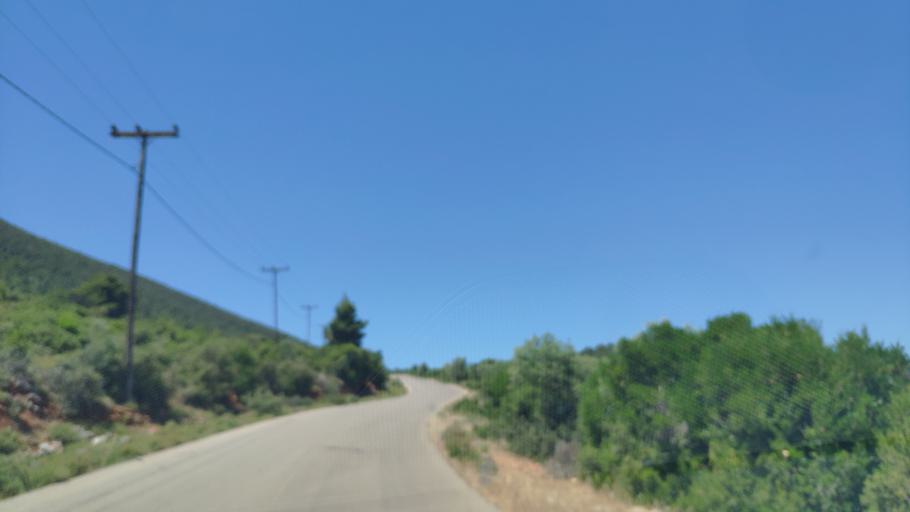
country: GR
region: Central Greece
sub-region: Nomos Voiotias
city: Kaparellion
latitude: 38.2083
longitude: 23.1799
